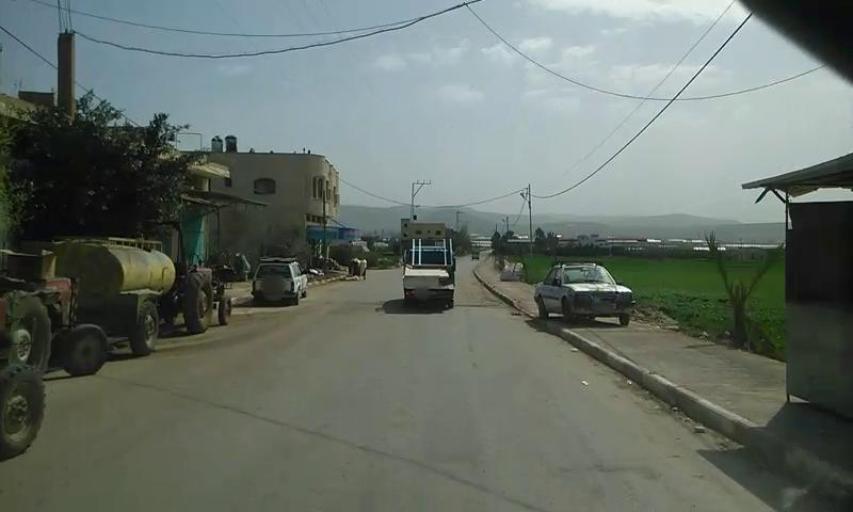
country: PS
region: West Bank
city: Birqin
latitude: 32.4472
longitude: 35.2619
